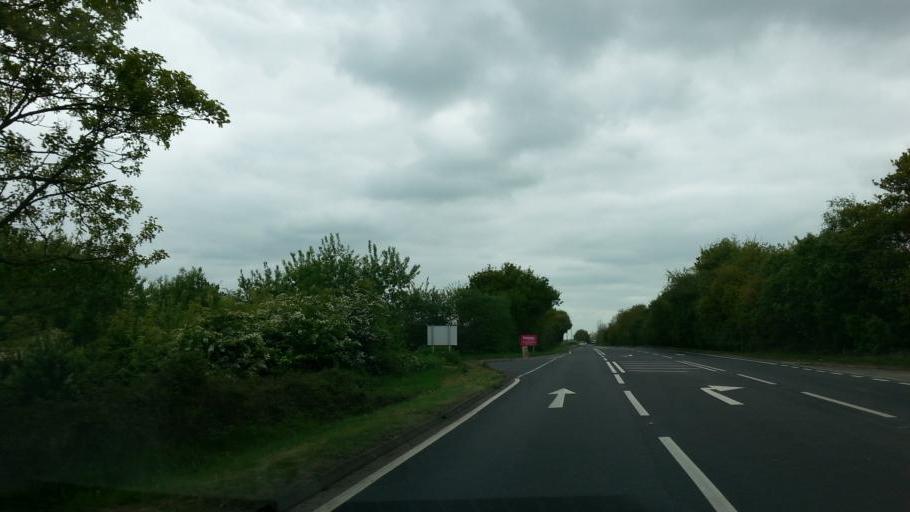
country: GB
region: England
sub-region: Suffolk
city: Hadleigh
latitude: 52.0530
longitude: 0.9947
